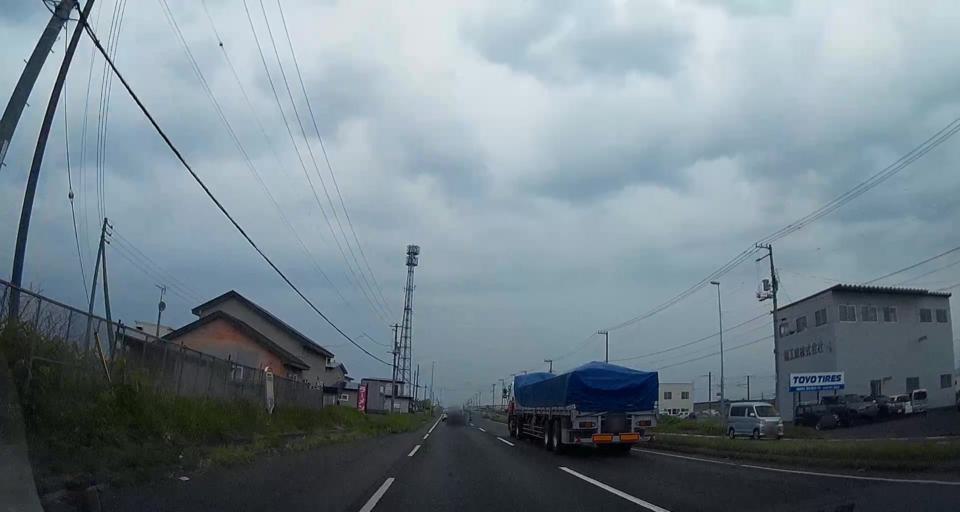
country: JP
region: Hokkaido
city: Tomakomai
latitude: 42.6080
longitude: 141.5049
